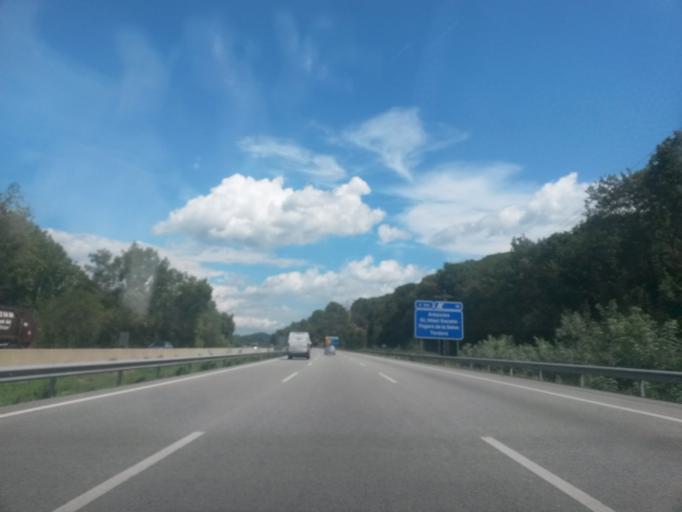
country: ES
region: Catalonia
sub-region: Provincia de Girona
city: Hostalric
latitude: 41.7259
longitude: 2.6000
